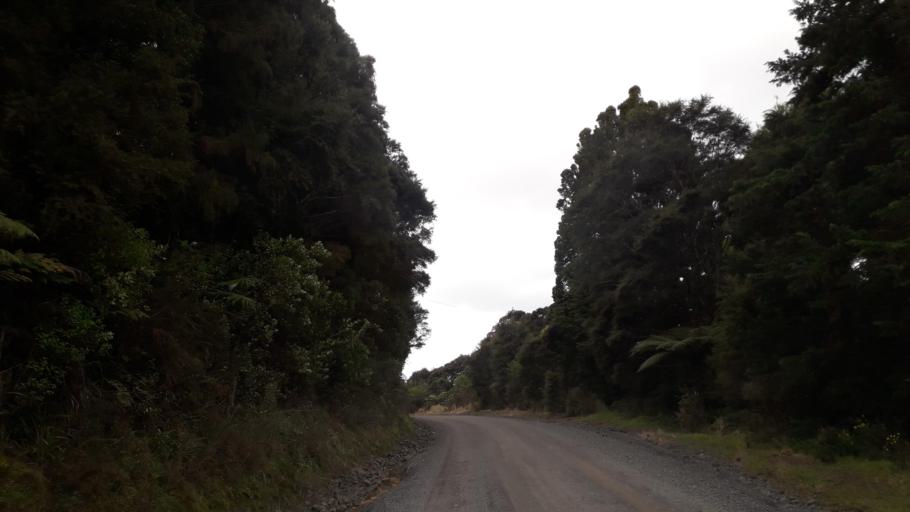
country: NZ
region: Northland
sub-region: Far North District
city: Paihia
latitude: -35.3248
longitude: 174.2342
